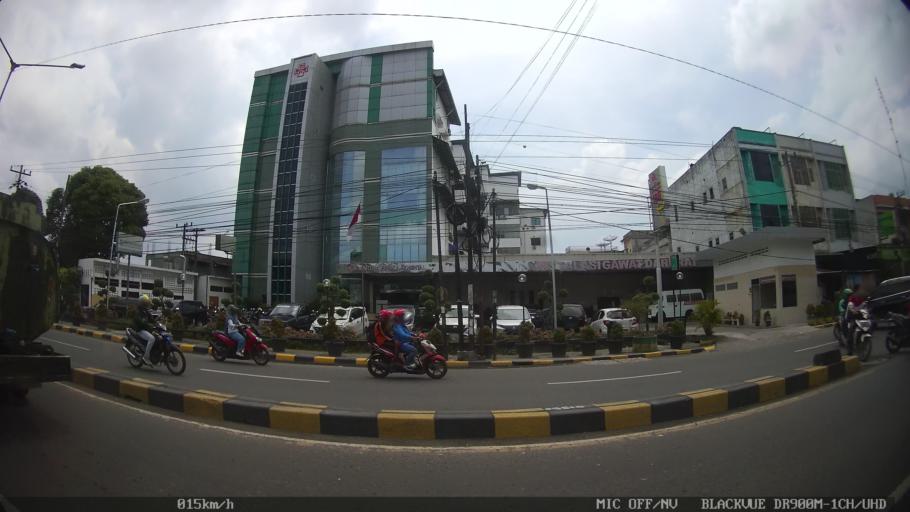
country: ID
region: North Sumatra
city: Medan
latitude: 3.6338
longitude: 98.6692
